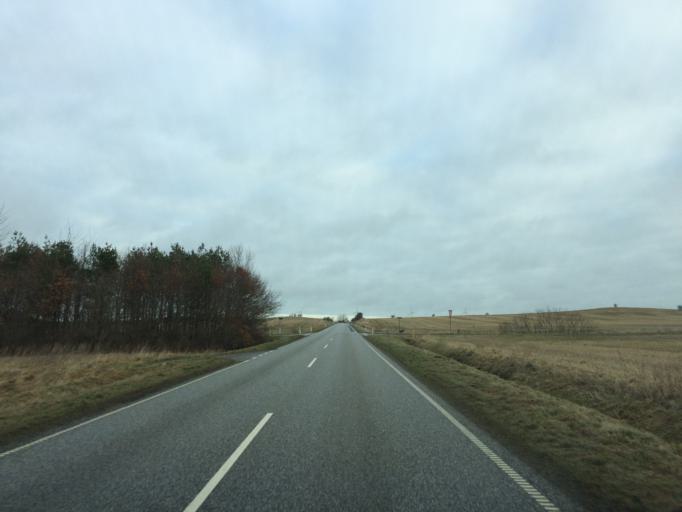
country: DK
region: Central Jutland
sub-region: Struer Kommune
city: Struer
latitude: 56.4105
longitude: 8.4767
